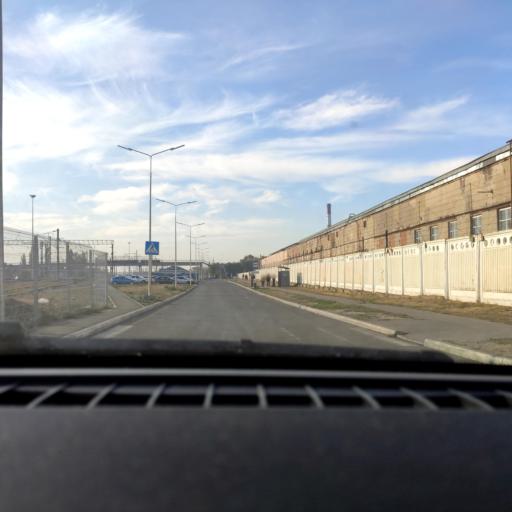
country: RU
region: Voronezj
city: Voronezh
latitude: 51.6384
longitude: 39.2574
